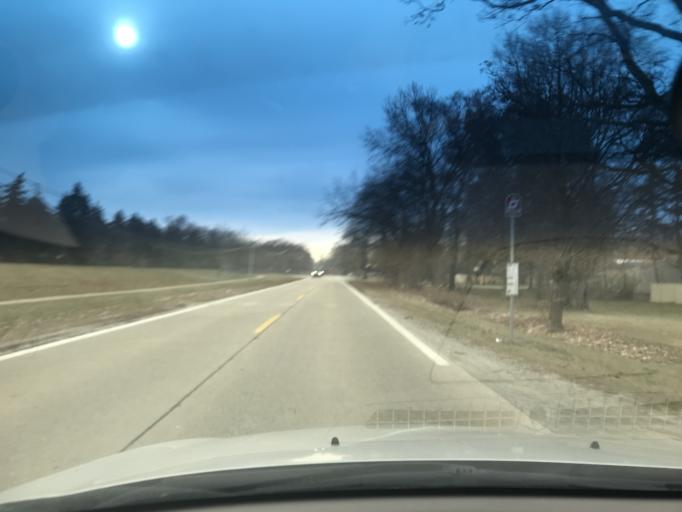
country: US
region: Michigan
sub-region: Macomb County
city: Shelby
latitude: 42.6619
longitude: -83.0533
